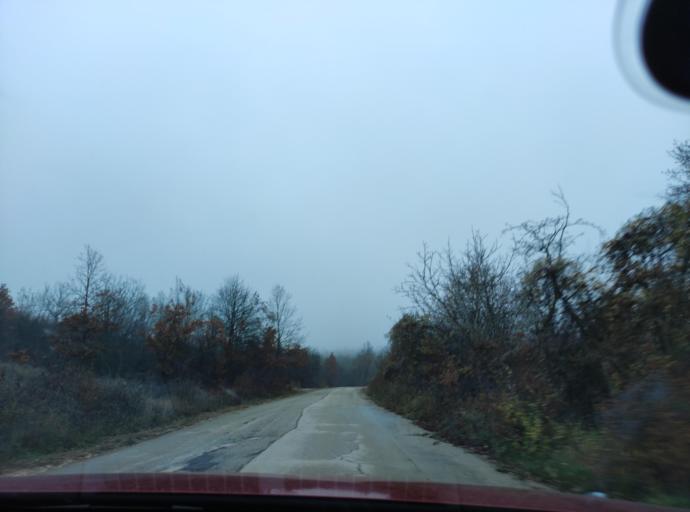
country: BG
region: Lovech
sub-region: Obshtina Yablanitsa
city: Yablanitsa
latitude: 43.1111
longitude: 24.0681
